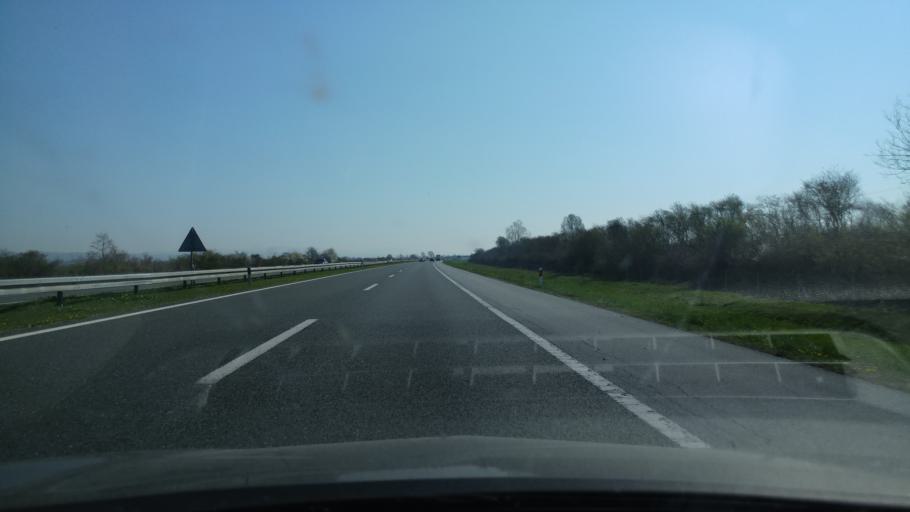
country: HR
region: Brodsko-Posavska
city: Okucani
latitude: 45.2332
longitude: 17.2609
